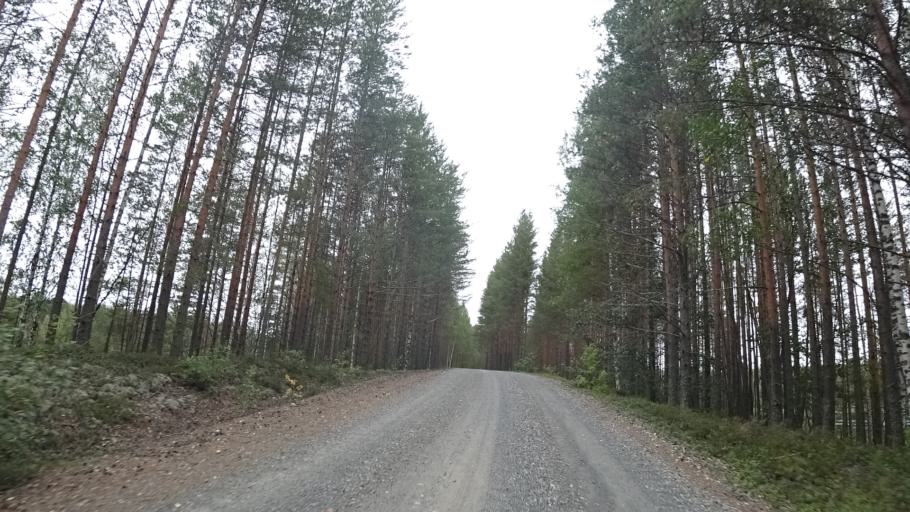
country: FI
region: North Karelia
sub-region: Joensuu
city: Ilomantsi
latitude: 62.6180
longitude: 31.1952
